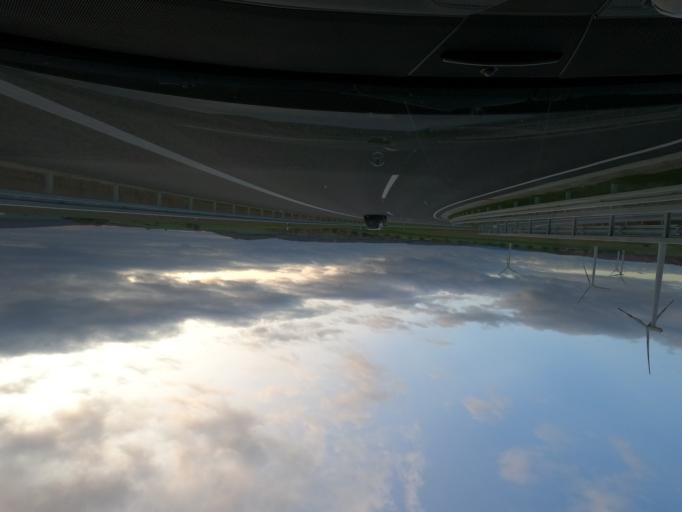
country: DE
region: Lower Saxony
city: Holle
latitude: 52.0865
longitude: 10.1790
